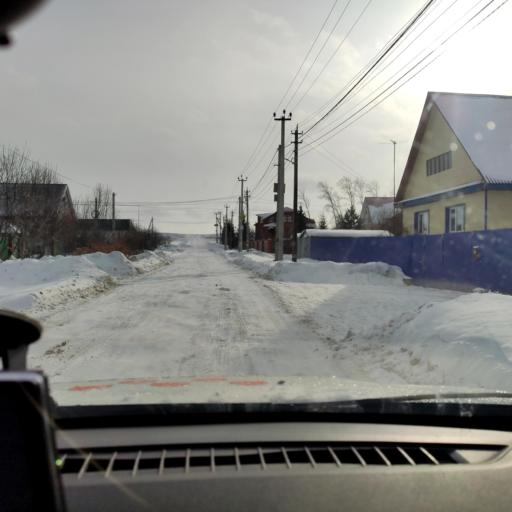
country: RU
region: Bashkortostan
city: Avdon
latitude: 54.6082
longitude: 55.8565
